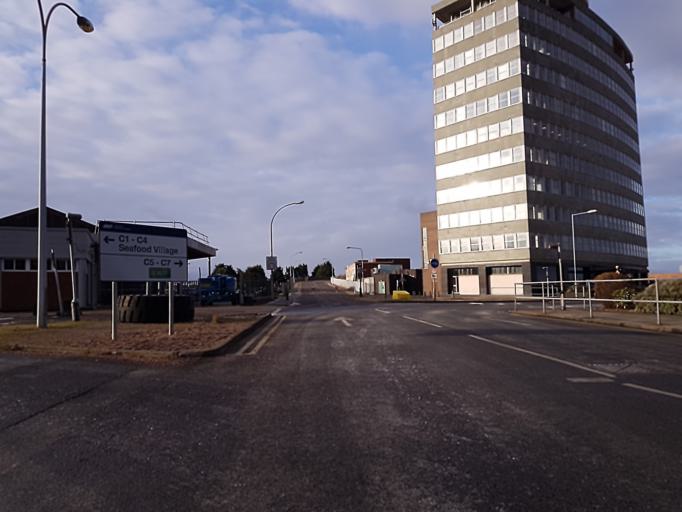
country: GB
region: England
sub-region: North East Lincolnshire
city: Grimsby
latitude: 53.5767
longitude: -0.0594
